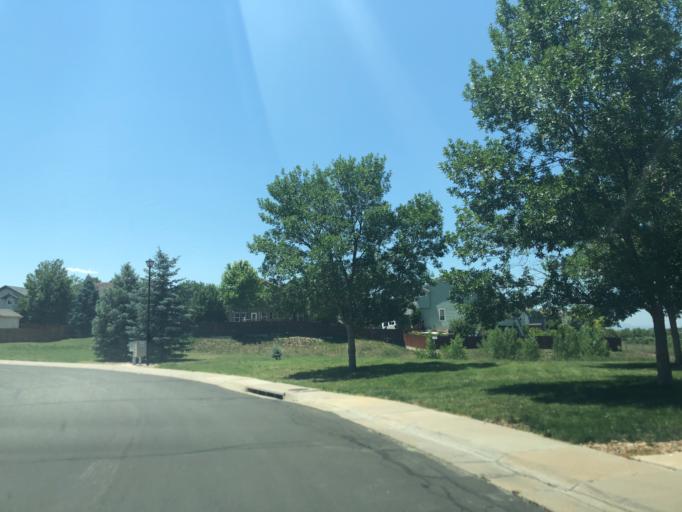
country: US
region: Colorado
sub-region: Arapahoe County
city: Dove Valley
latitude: 39.6311
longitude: -104.7640
